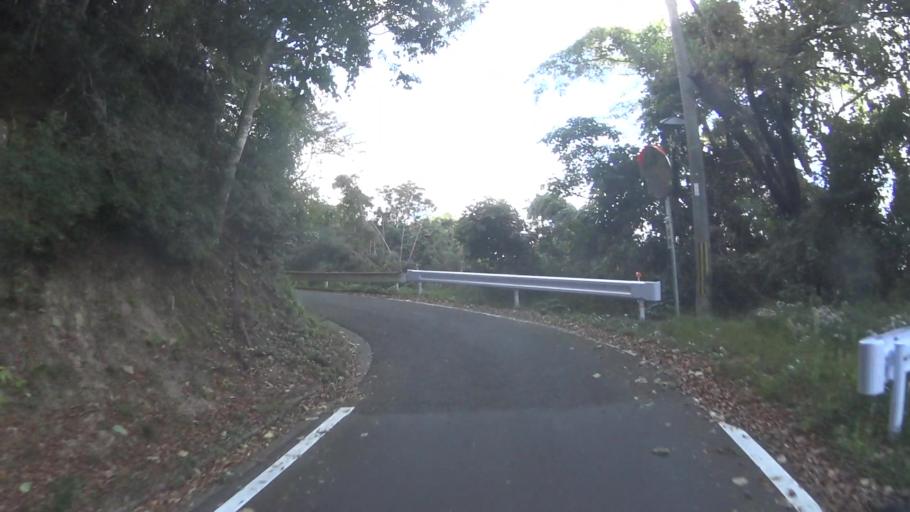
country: JP
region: Kyoto
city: Maizuru
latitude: 35.5681
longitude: 135.4144
